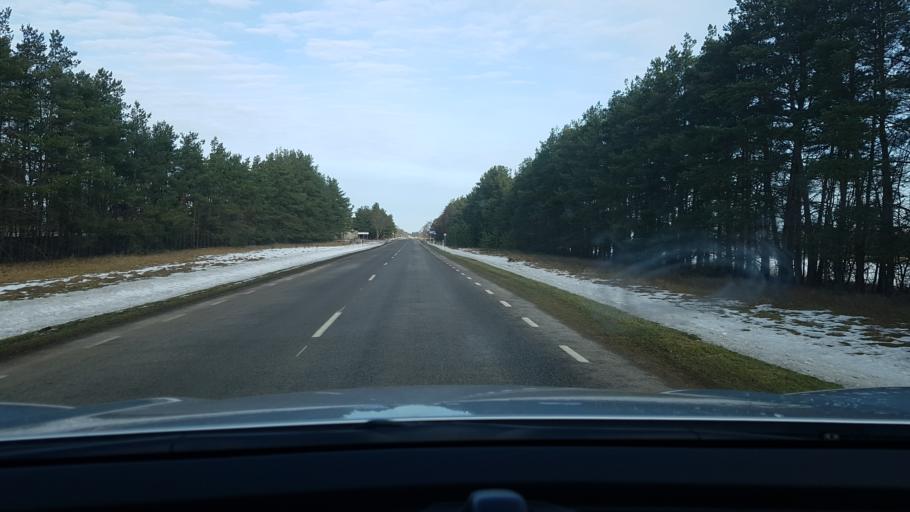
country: EE
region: Saare
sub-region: Kuressaare linn
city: Kuressaare
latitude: 58.5115
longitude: 22.7057
